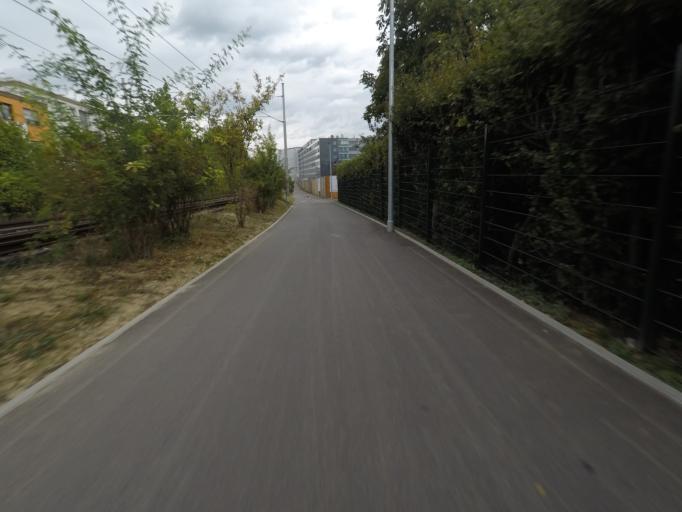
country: DE
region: Baden-Wuerttemberg
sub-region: Regierungsbezirk Stuttgart
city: Leinfelden-Echterdingen
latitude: 48.7059
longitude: 9.1434
